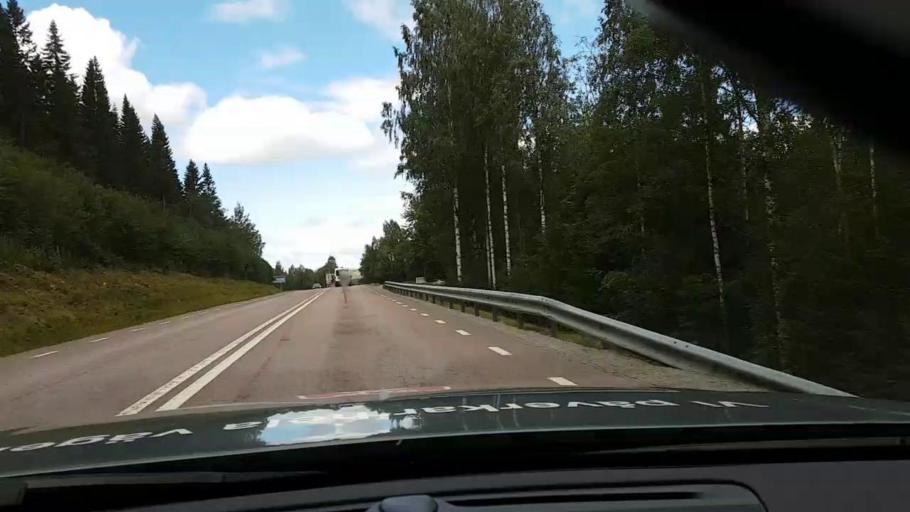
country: SE
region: Vaesternorrland
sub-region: OErnskoeldsviks Kommun
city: Bjasta
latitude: 63.3610
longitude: 18.4640
